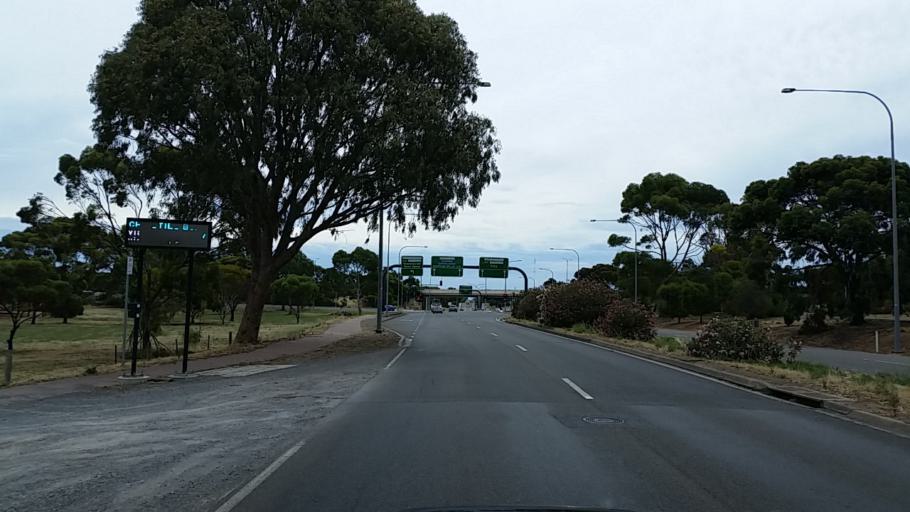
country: AU
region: South Australia
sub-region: Onkaparinga
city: Reynella
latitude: -35.1058
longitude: 138.5132
